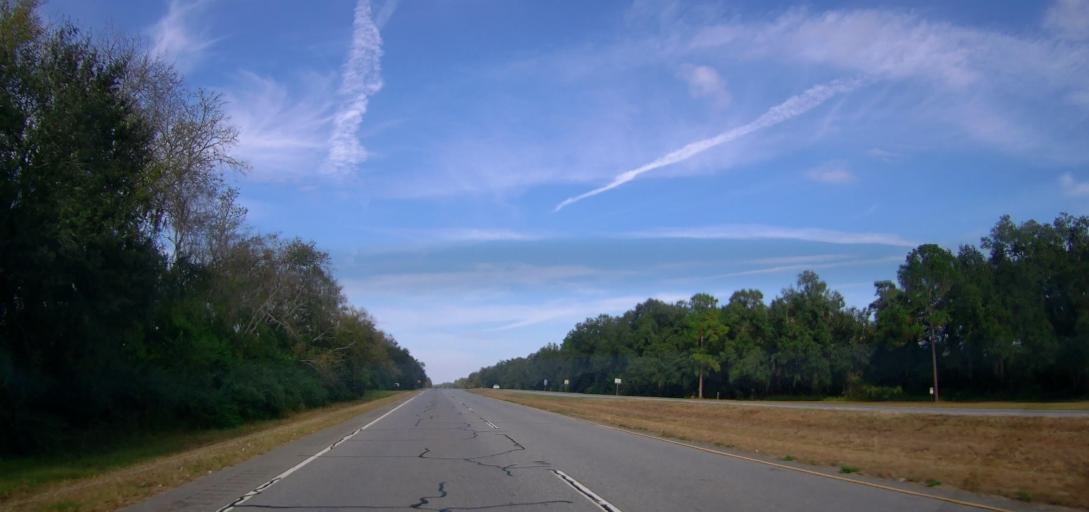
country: US
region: Georgia
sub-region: Mitchell County
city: Camilla
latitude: 31.3012
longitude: -84.1809
